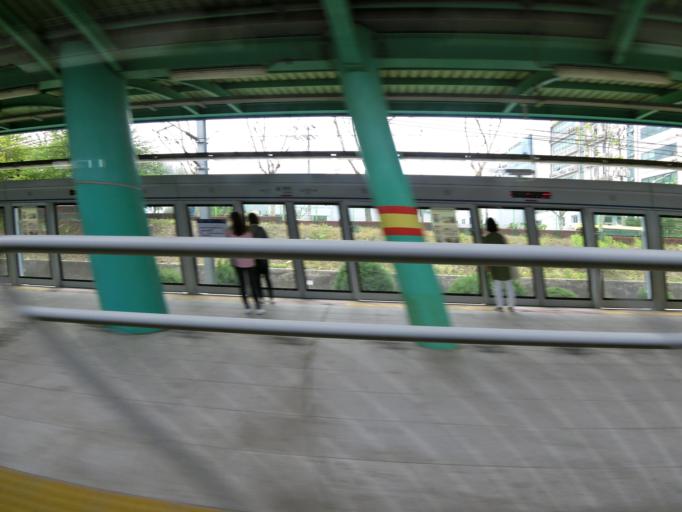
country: KR
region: Gyeonggi-do
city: Anyang-si
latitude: 37.3840
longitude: 126.9356
